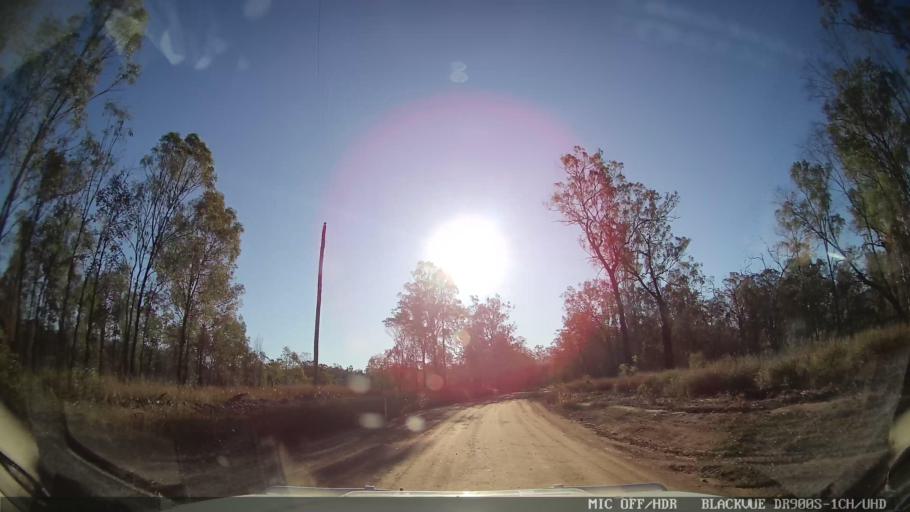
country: AU
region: Queensland
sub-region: Bundaberg
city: Sharon
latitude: -24.7402
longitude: 151.5259
